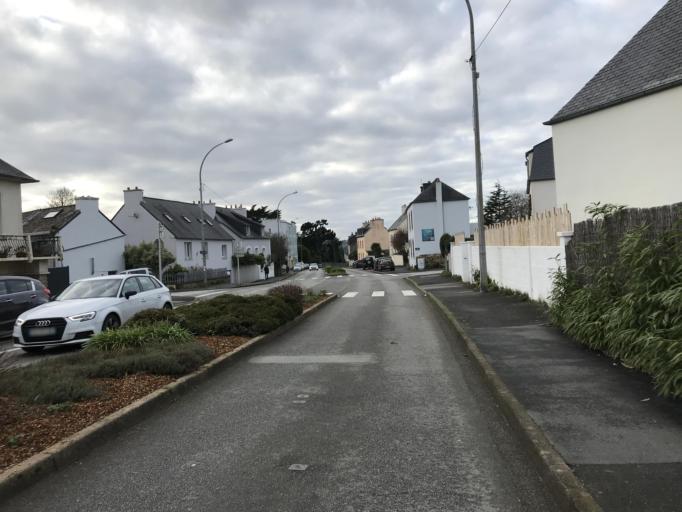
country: FR
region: Brittany
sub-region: Departement du Finistere
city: Le Relecq-Kerhuon
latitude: 48.3953
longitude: -4.4115
